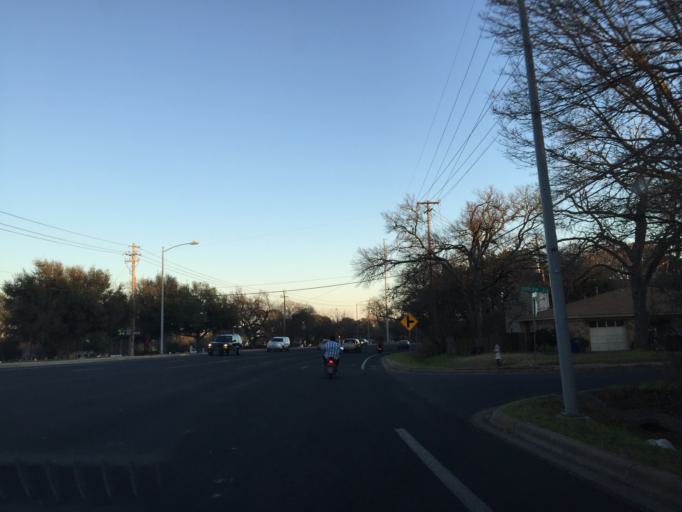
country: US
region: Texas
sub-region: Williamson County
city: Jollyville
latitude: 30.4272
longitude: -97.7595
